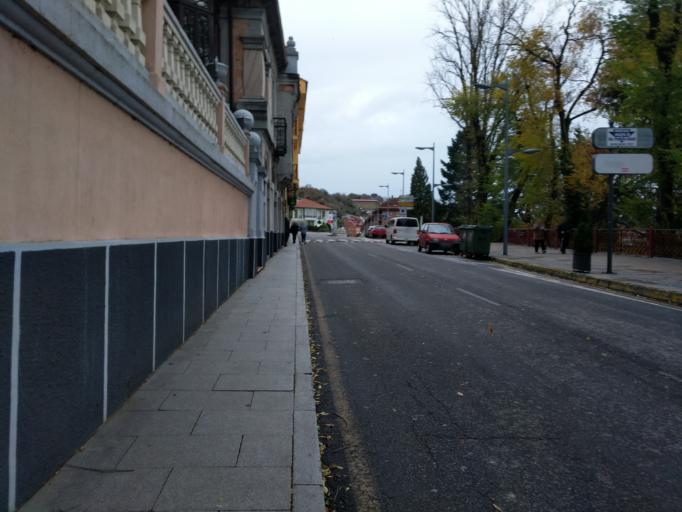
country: ES
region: Asturias
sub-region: Province of Asturias
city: Tineo
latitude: 43.3345
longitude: -6.4150
